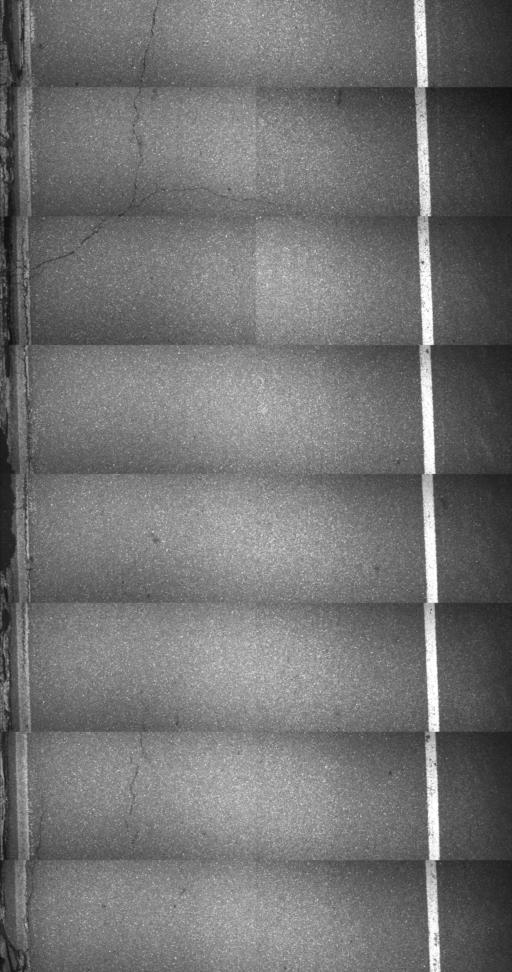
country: US
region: New Hampshire
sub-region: Coos County
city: Colebrook
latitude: 45.0062
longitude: -71.5976
